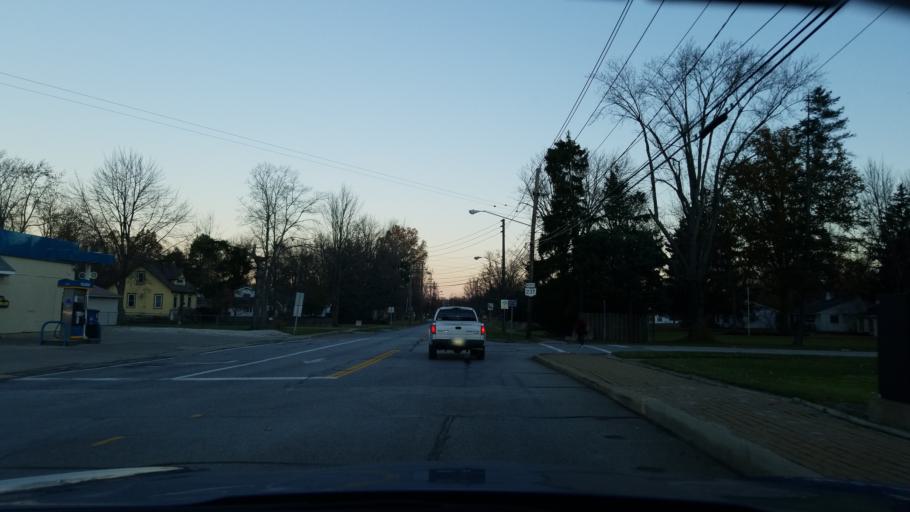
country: US
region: Ohio
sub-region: Cuyahoga County
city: Berea
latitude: 41.3507
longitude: -81.8576
